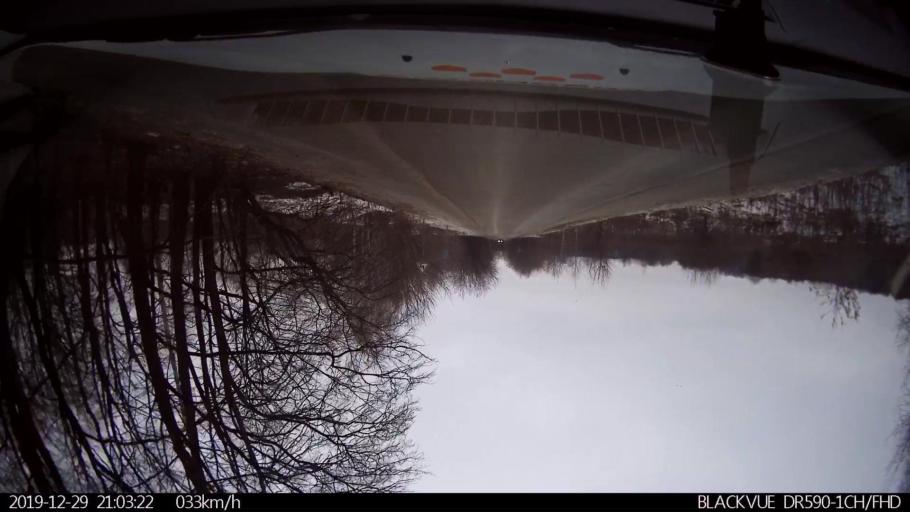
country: RU
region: Nizjnij Novgorod
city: Afonino
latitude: 56.1948
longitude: 44.0054
